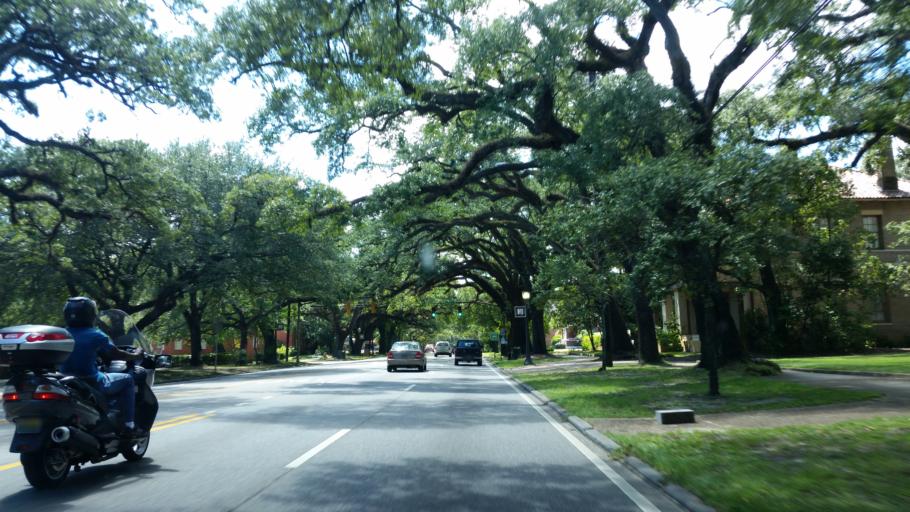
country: US
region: Alabama
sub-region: Mobile County
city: Mobile
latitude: 30.6848
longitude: -88.0585
